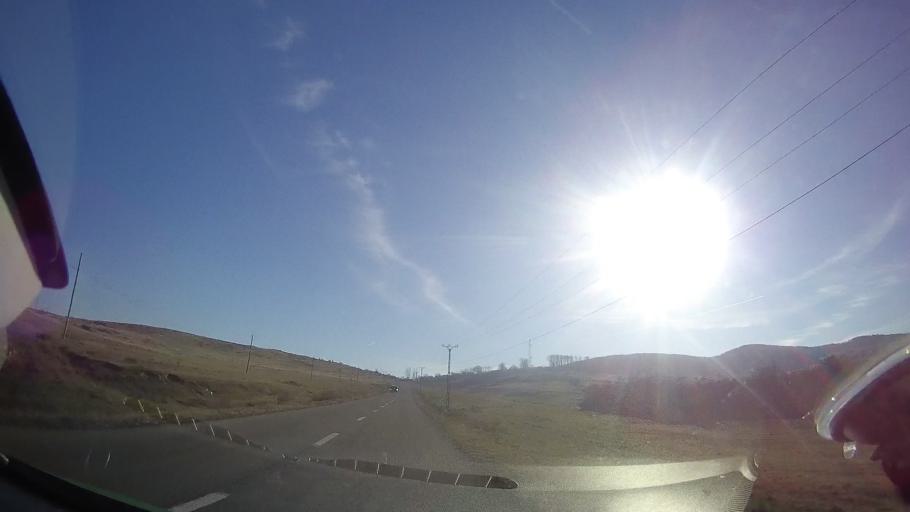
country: RO
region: Bihor
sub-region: Comuna Vadu Crisului
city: Vadu Crisului
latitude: 46.9818
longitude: 22.5309
